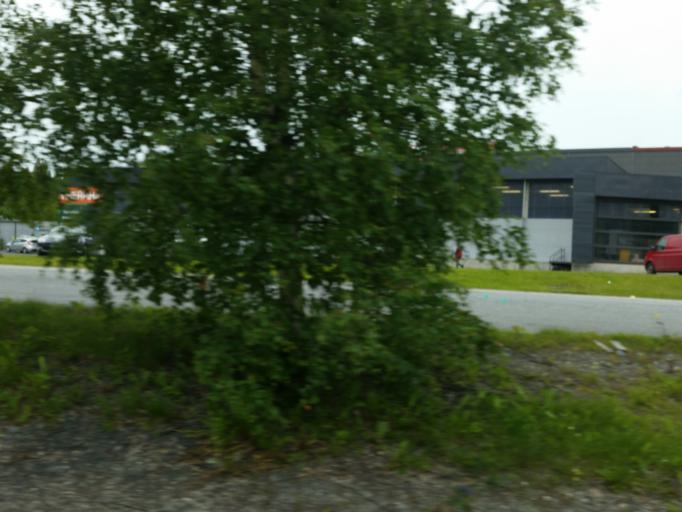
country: FI
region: Northern Savo
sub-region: Kuopio
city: Kuopio
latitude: 62.8715
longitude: 27.6244
